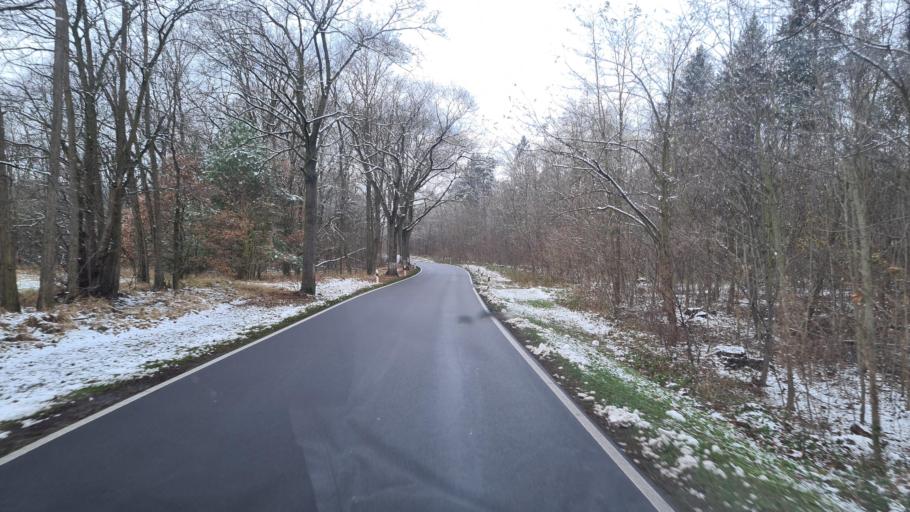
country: DE
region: Brandenburg
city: Rehfelde
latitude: 52.5384
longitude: 13.9316
